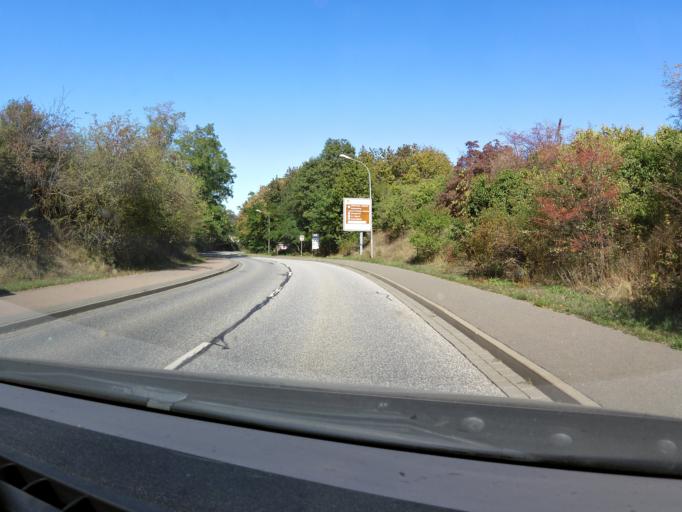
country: DE
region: Saxony-Anhalt
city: Quedlinburg
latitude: 51.7731
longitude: 11.1405
